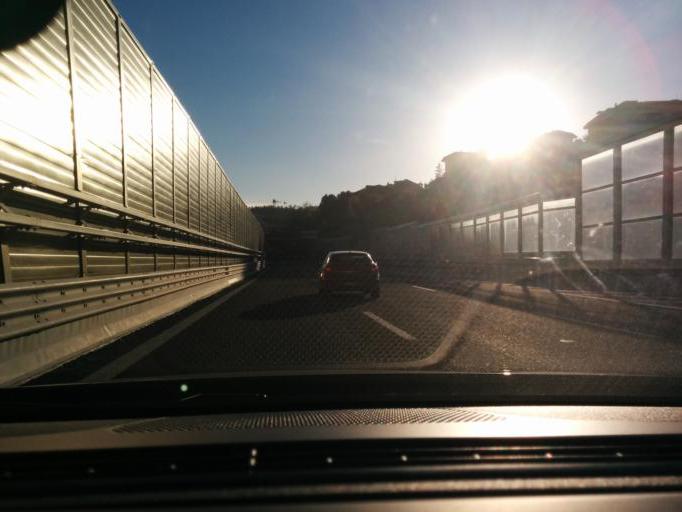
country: IT
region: Liguria
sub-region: Provincia di Genova
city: Arenzano
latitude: 44.4043
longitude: 8.6720
